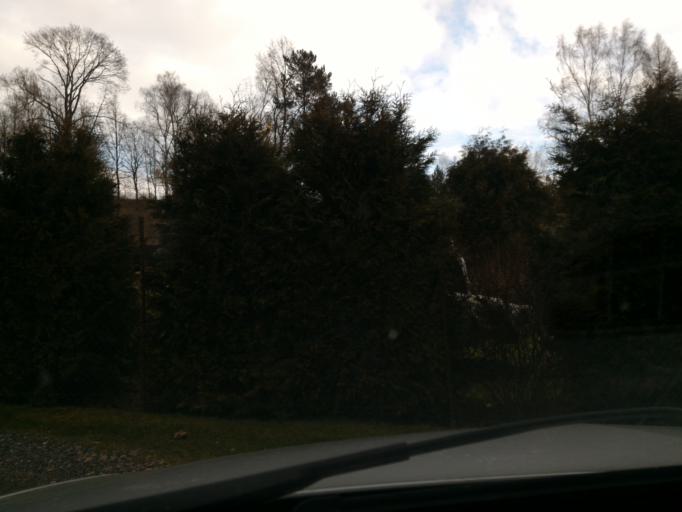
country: DE
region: Saxony
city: Grossschonau
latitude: 50.9006
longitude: 14.6793
